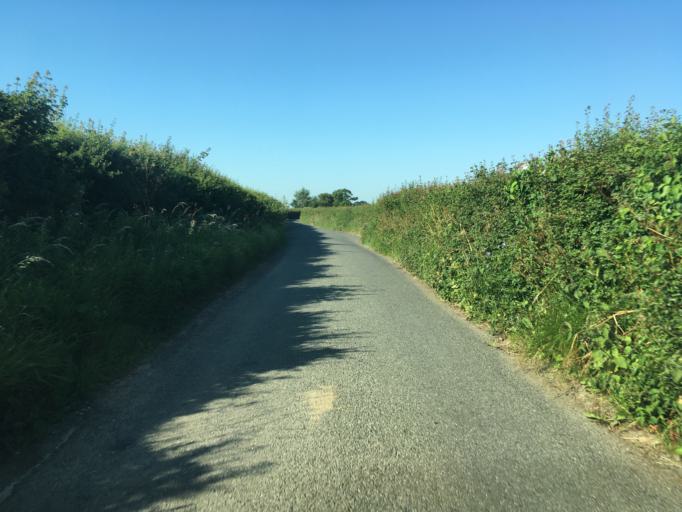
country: GB
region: England
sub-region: South Gloucestershire
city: Hinton
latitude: 51.4775
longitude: -2.3919
